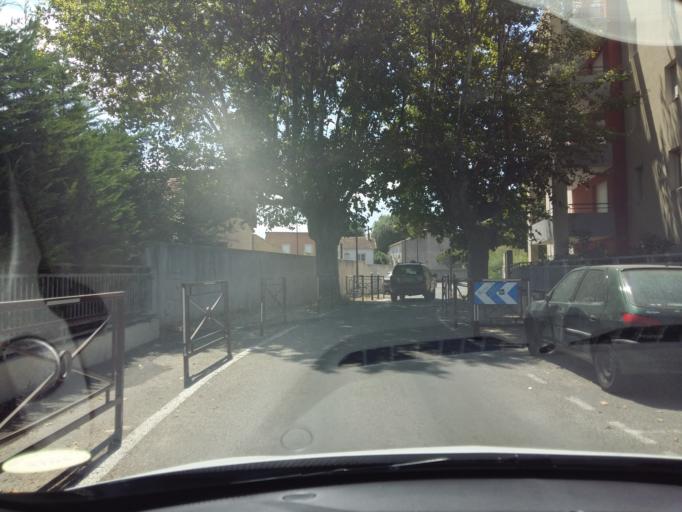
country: FR
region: Provence-Alpes-Cote d'Azur
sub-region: Departement du Vaucluse
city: Le Pontet
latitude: 43.9546
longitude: 4.8347
